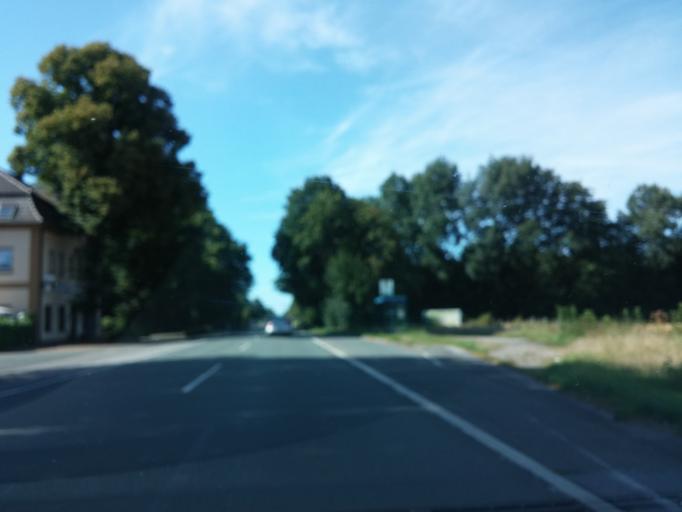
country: DE
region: North Rhine-Westphalia
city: Dorsten
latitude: 51.6486
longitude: 6.9834
